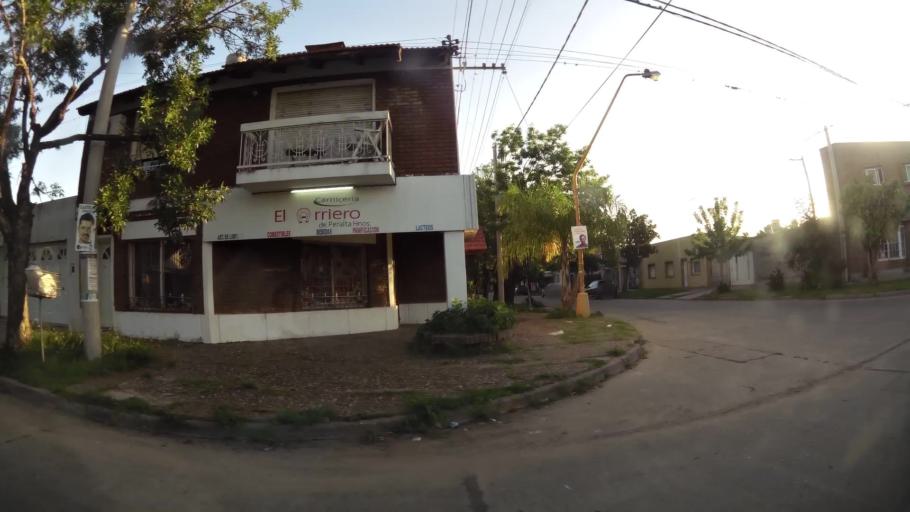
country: AR
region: Santa Fe
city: Santa Fe de la Vera Cruz
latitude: -31.6013
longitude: -60.6825
